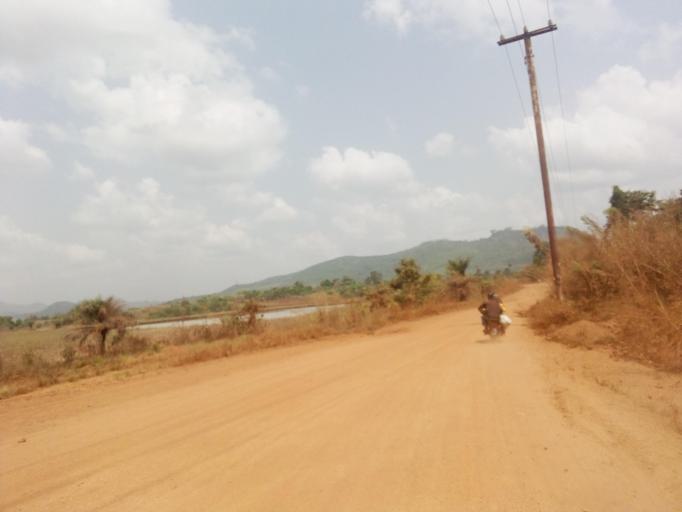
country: SL
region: Southern Province
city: Mogbwemo
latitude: 7.6667
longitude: -12.2789
